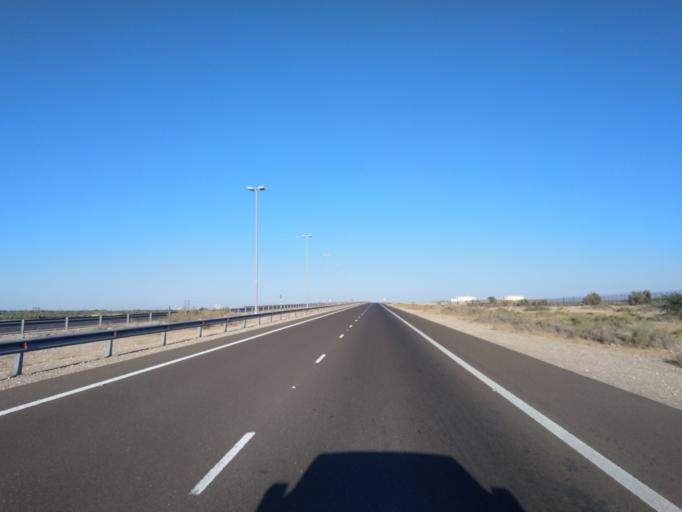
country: OM
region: Al Buraimi
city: Al Buraymi
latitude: 24.5350
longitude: 55.5843
